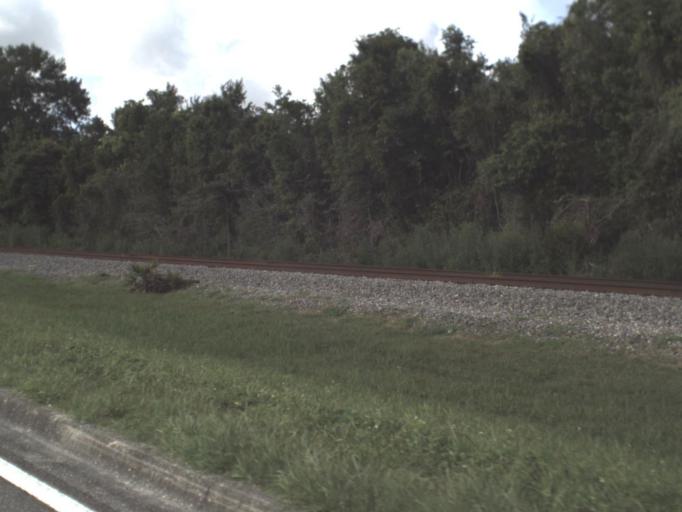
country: US
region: Florida
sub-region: Hillsborough County
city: Lutz
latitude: 28.1752
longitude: -82.4631
